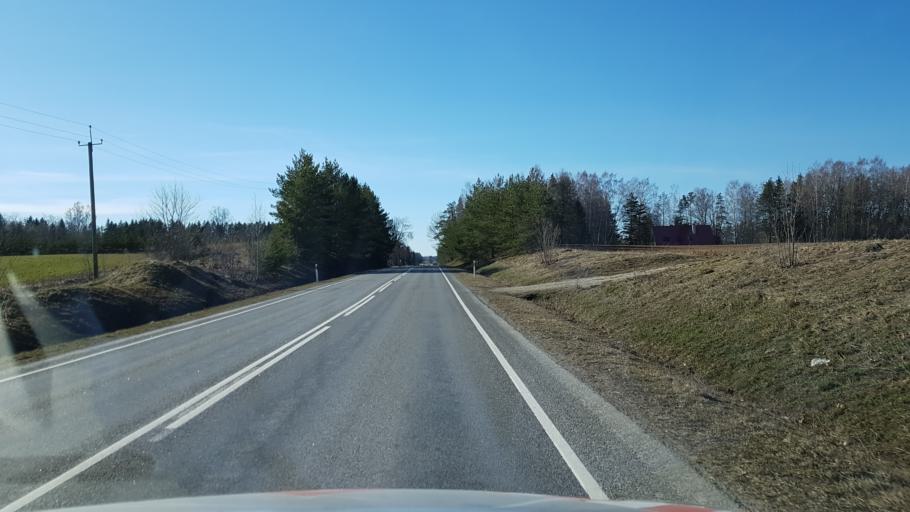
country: EE
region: Laeaene-Virumaa
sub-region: Vinni vald
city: Vinni
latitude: 59.3267
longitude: 26.4212
